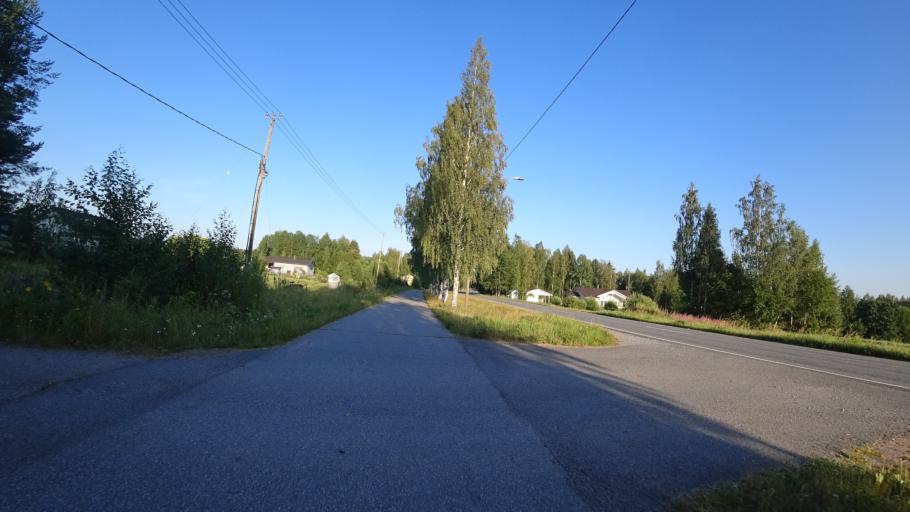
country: FI
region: Pirkanmaa
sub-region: Tampere
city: Nokia
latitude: 61.4700
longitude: 23.3920
